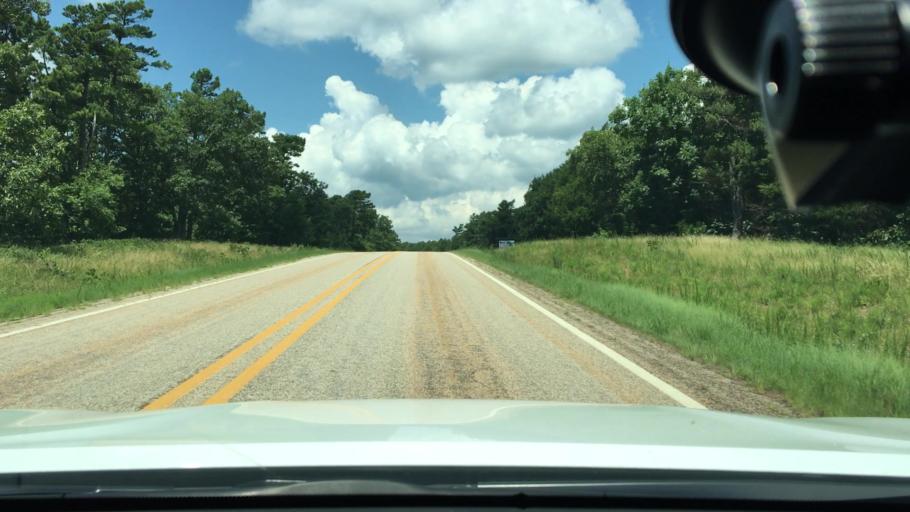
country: US
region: Arkansas
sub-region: Logan County
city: Paris
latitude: 35.1764
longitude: -93.5987
